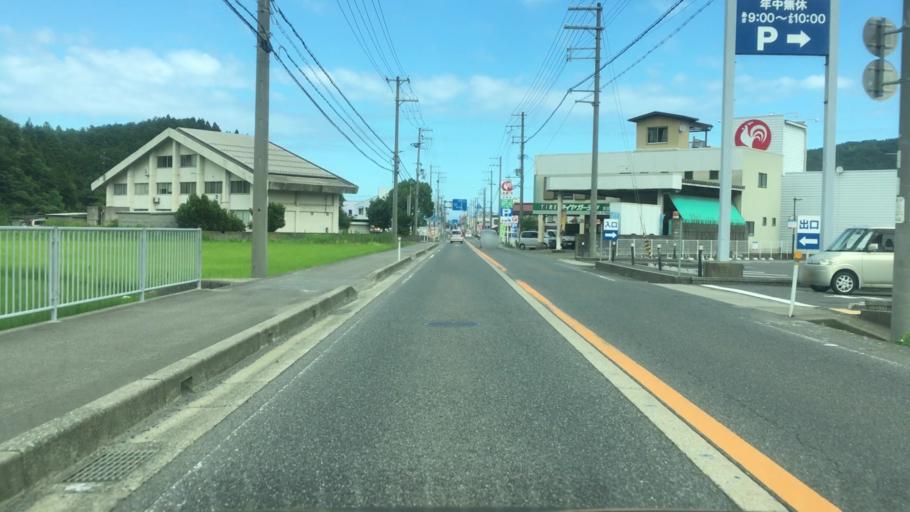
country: JP
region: Tottori
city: Tottori
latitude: 35.6156
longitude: 134.4652
